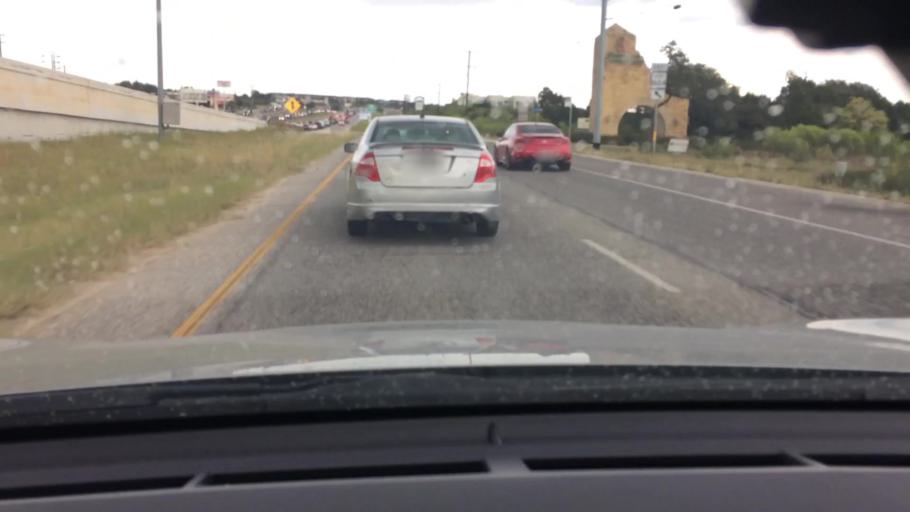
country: US
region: Texas
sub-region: Bexar County
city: Shavano Park
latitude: 29.5939
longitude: -98.5736
